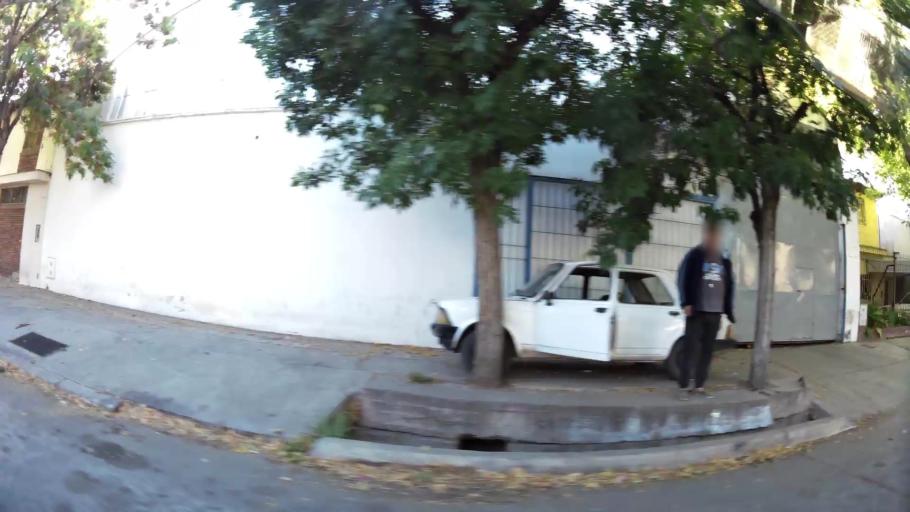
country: AR
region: Mendoza
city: Mendoza
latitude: -32.8717
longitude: -68.8198
